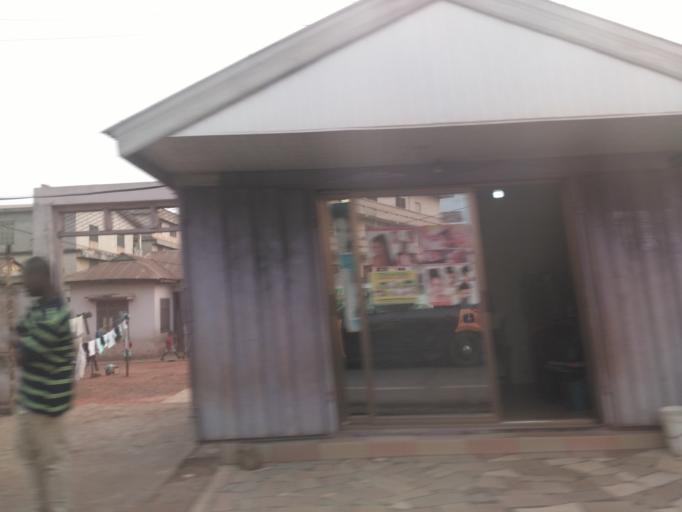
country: GH
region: Ashanti
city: Tafo
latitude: 6.7109
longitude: -1.6132
